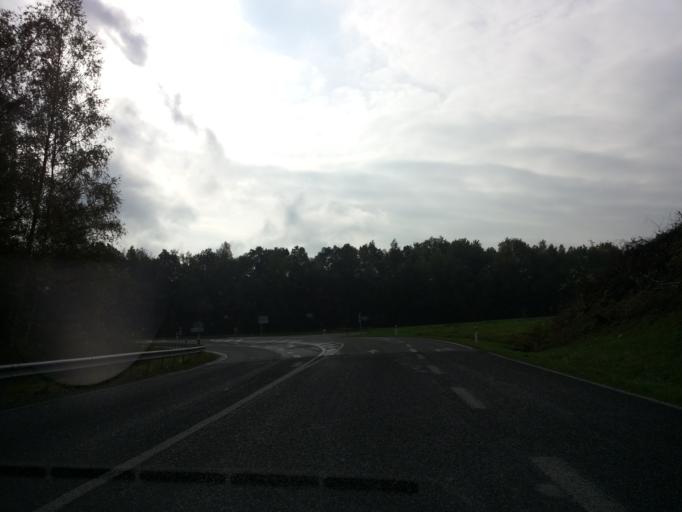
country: FR
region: Lorraine
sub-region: Departement de la Meuse
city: Montmedy
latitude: 49.4671
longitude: 5.3981
